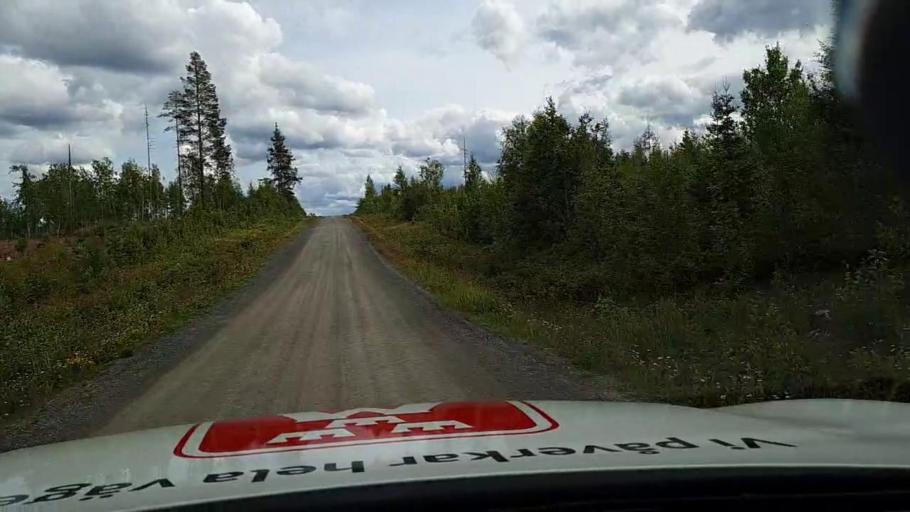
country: SE
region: Jaemtland
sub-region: OEstersunds Kommun
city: Lit
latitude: 63.2952
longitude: 15.3353
